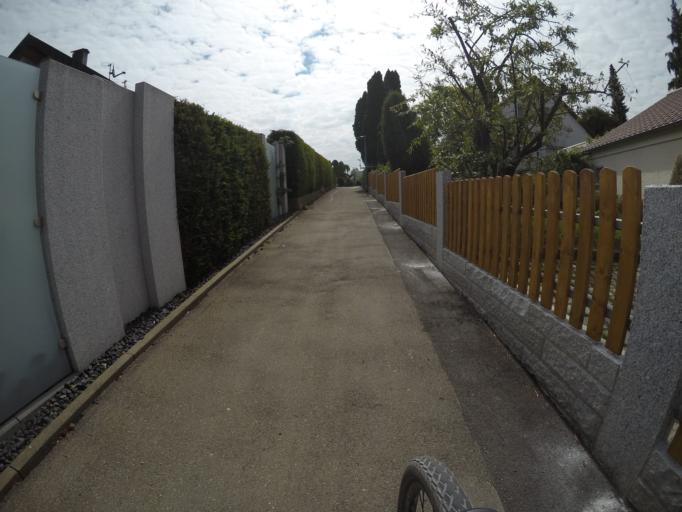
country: DE
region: Baden-Wuerttemberg
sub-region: Regierungsbezirk Stuttgart
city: Kirchheim unter Teck
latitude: 48.6439
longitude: 9.4415
